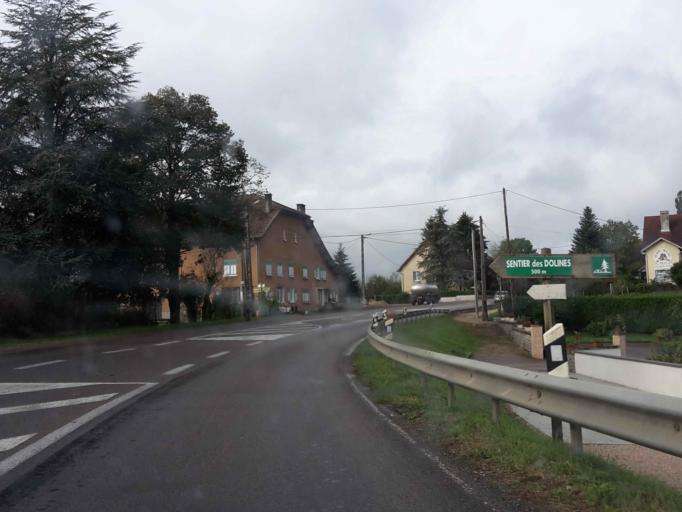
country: FR
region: Franche-Comte
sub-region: Departement du Doubs
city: Roulans
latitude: 47.3367
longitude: 6.2835
